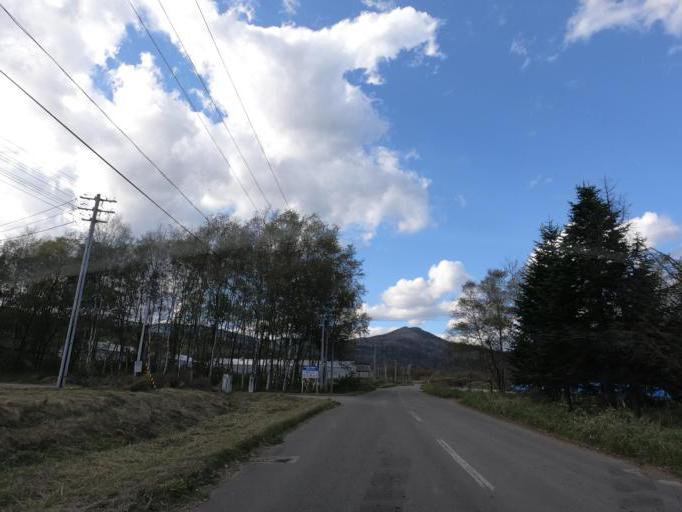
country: JP
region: Hokkaido
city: Otofuke
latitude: 43.2869
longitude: 143.2327
